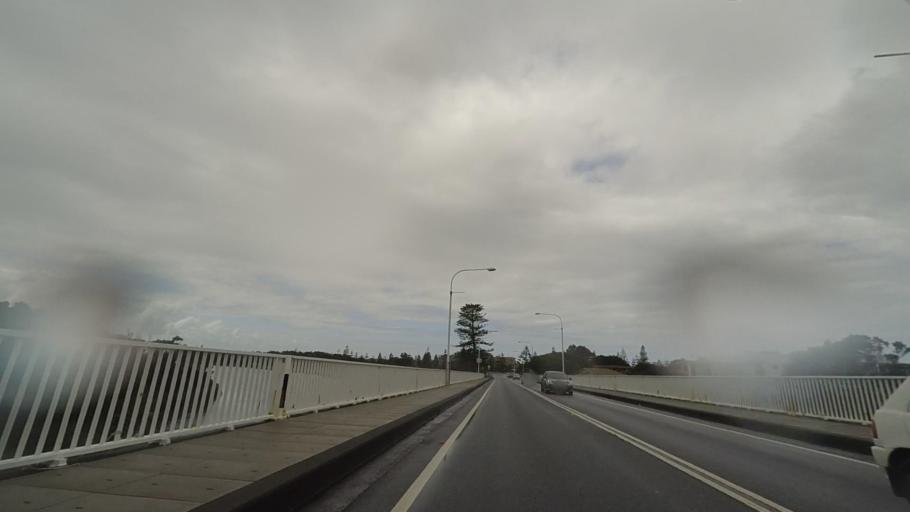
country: AU
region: New South Wales
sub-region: Wyong Shire
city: The Entrance
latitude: -33.3369
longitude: 151.5011
